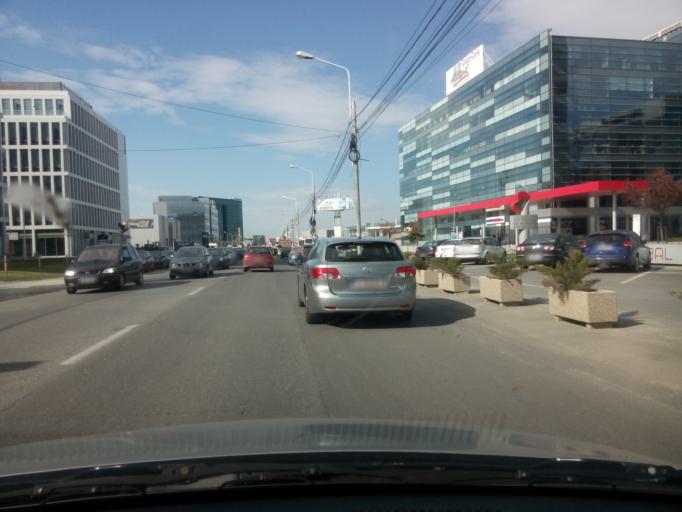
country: RO
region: Ilfov
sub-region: Voluntari City
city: Voluntari
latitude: 44.4886
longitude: 26.1264
